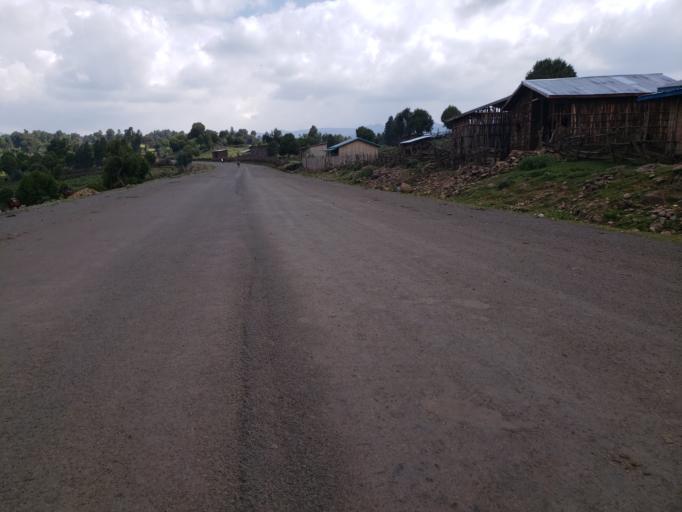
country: ET
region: Oromiya
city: Dodola
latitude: 6.8753
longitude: 39.3856
